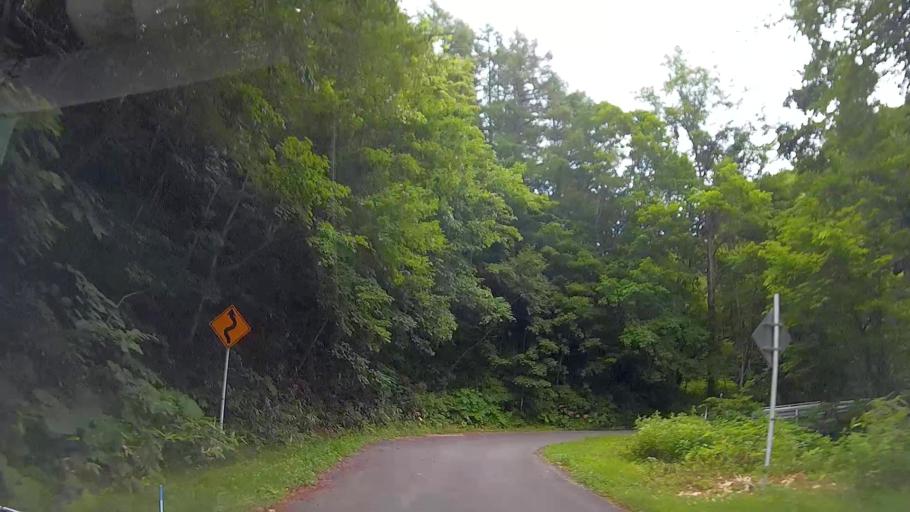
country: JP
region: Hokkaido
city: Nanae
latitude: 42.0464
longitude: 140.4895
